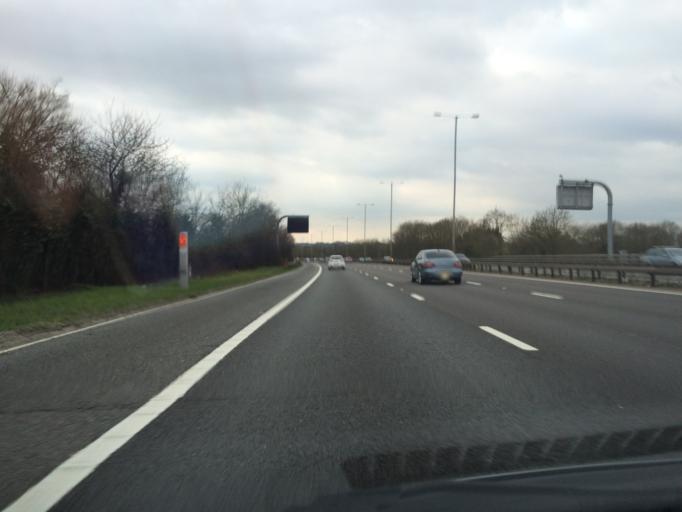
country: GB
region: England
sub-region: Wokingham
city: Winnersh
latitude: 51.4246
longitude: -0.8894
